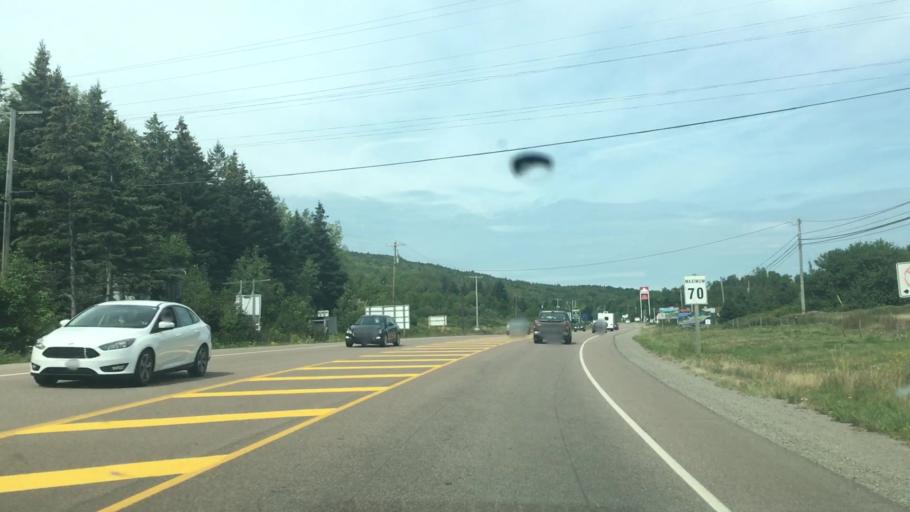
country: CA
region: Nova Scotia
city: Port Hawkesbury
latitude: 45.6498
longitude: -61.4412
